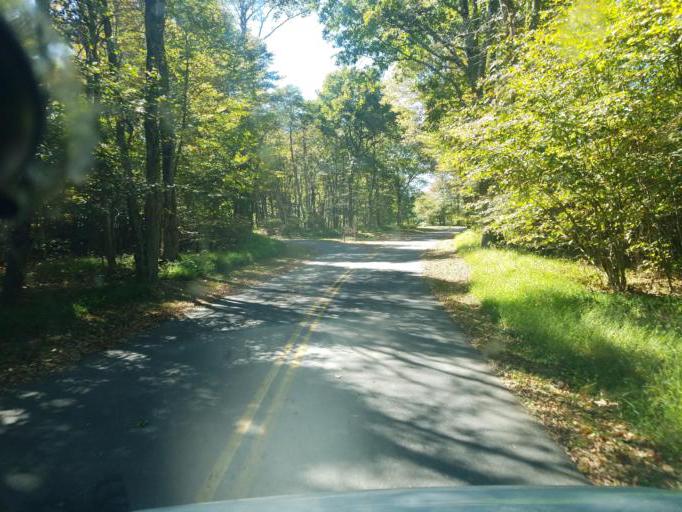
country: US
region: Virginia
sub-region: Rockingham County
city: Elkton
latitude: 38.3826
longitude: -78.5183
